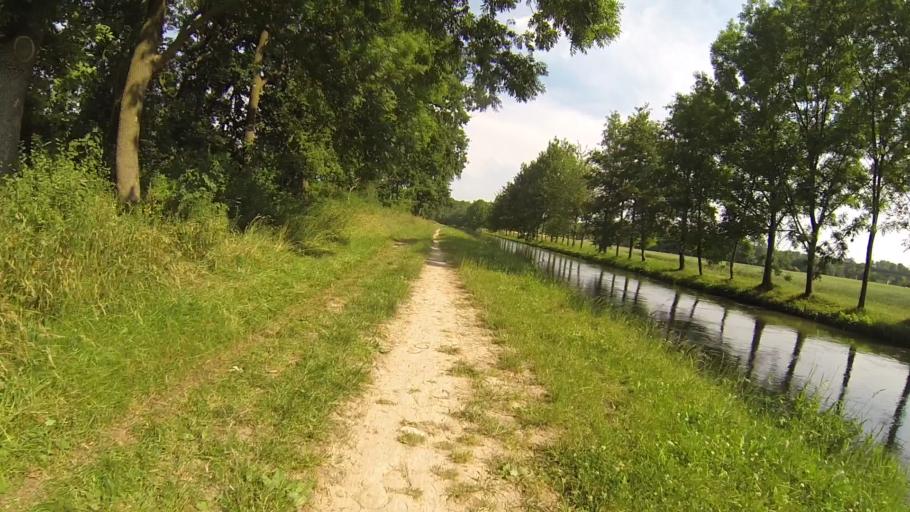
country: DE
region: Bavaria
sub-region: Swabia
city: Neu-Ulm
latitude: 48.3742
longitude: 9.9965
